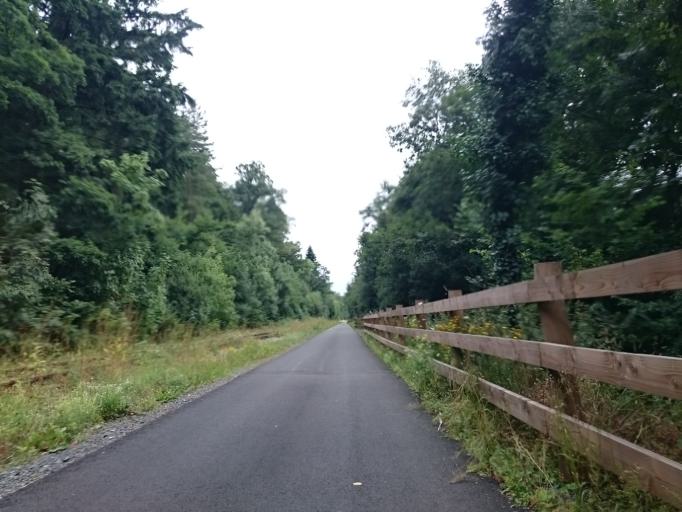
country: FR
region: Lower Normandy
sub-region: Departement du Calvados
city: Thury-Harcourt
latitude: 49.0225
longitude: -0.4651
